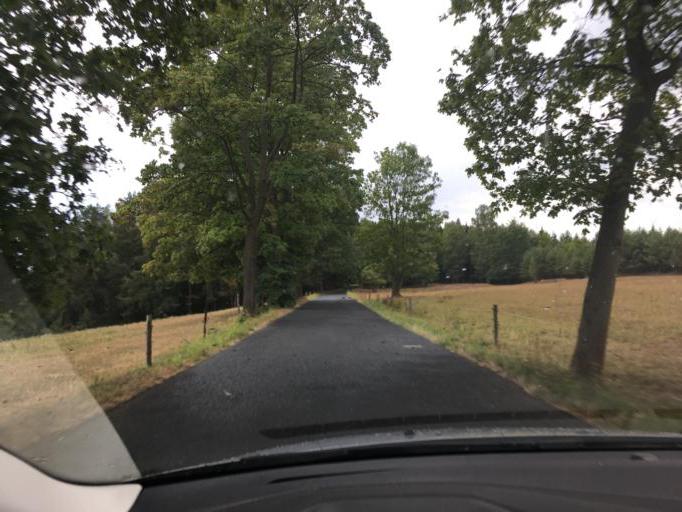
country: CZ
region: Ustecky
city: Benesov nad Ploucnici
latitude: 50.8174
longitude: 14.3349
